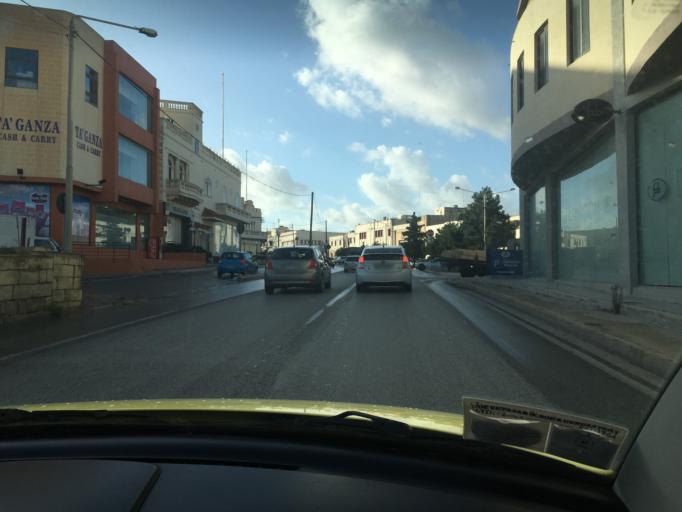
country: MT
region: Qormi
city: Qormi
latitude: 35.8750
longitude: 14.4677
